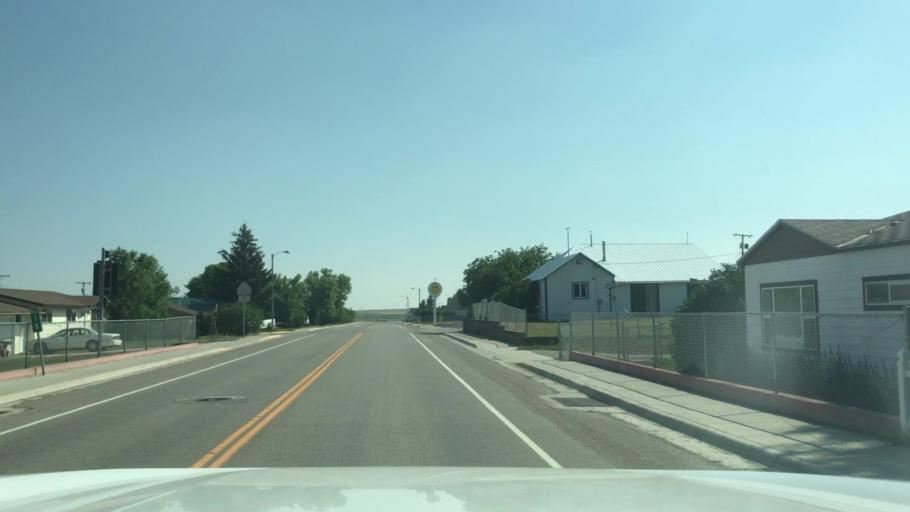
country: US
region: Montana
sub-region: Wheatland County
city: Harlowton
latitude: 46.6778
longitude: -109.7524
